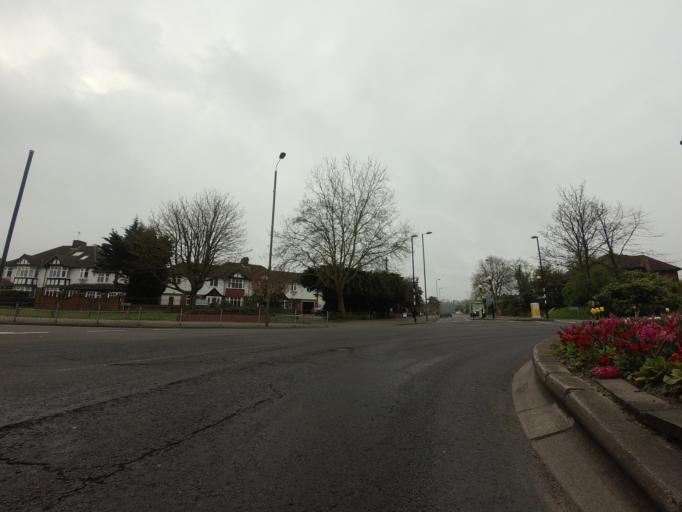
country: GB
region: England
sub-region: Greater London
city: Orpington
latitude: 51.3732
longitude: 0.0977
